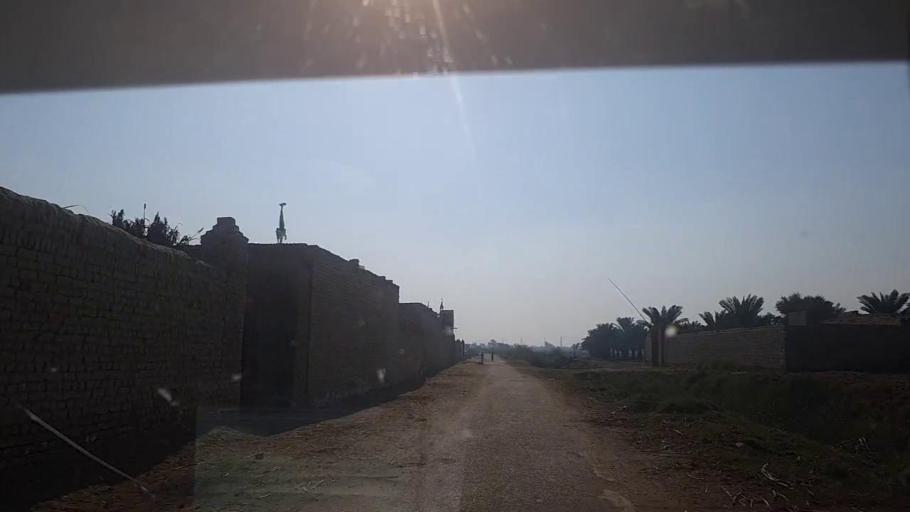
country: PK
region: Sindh
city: Gambat
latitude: 27.3654
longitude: 68.5590
